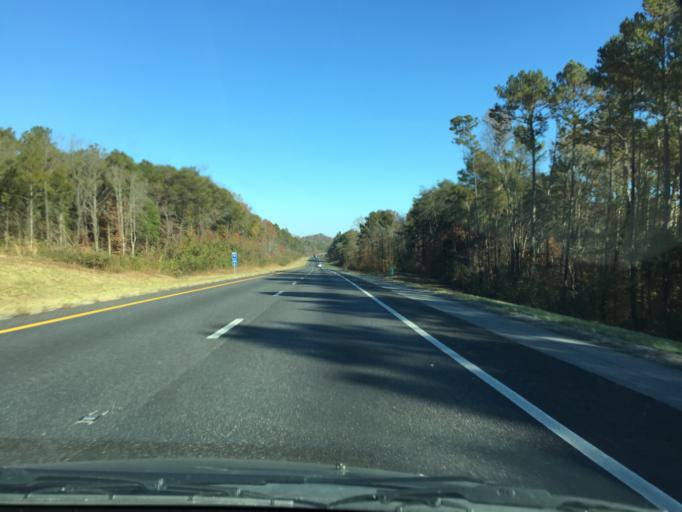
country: US
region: Tennessee
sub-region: Meigs County
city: Decatur
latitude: 35.3639
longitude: -84.7382
